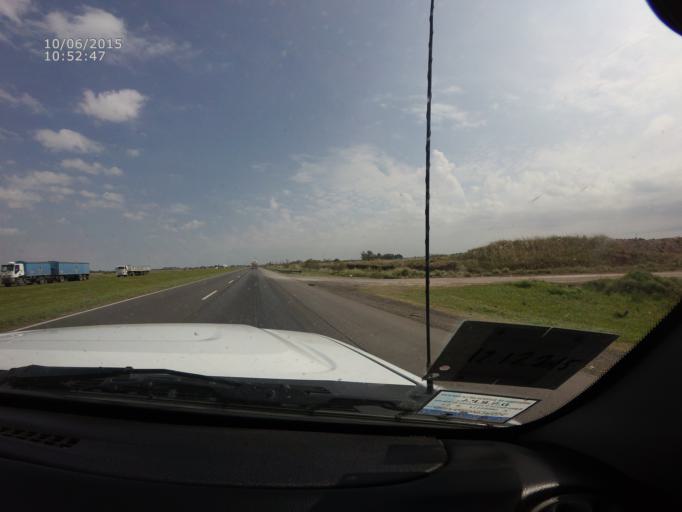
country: AR
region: Buenos Aires
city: San Nicolas de los Arroyos
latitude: -33.3485
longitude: -60.2756
